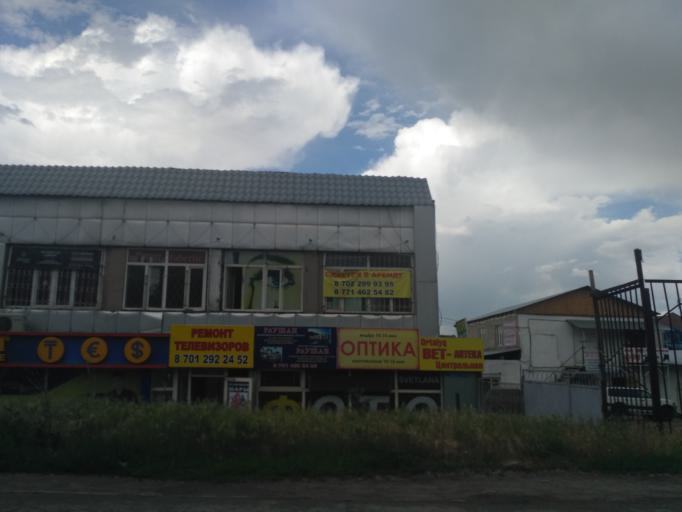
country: KZ
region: Almaty Oblysy
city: Burunday
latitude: 43.2013
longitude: 76.6278
